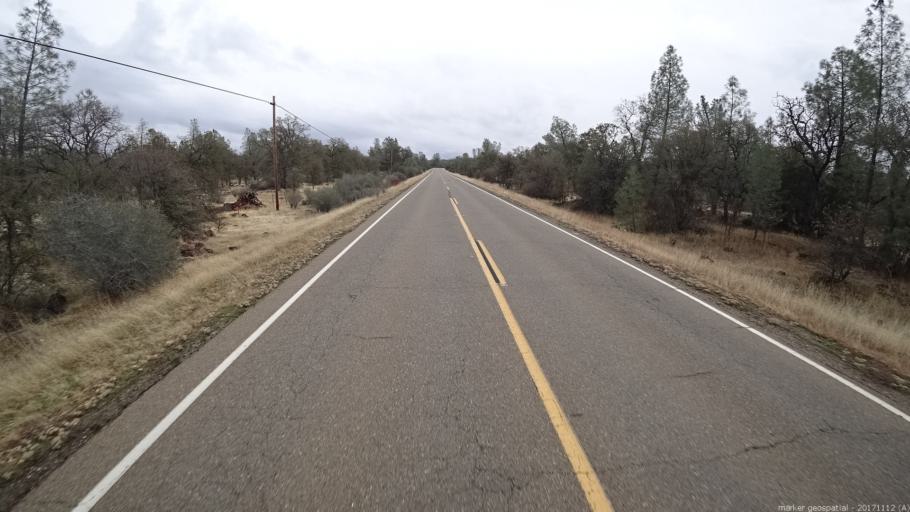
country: US
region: California
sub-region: Shasta County
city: Palo Cedro
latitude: 40.4835
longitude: -122.1109
